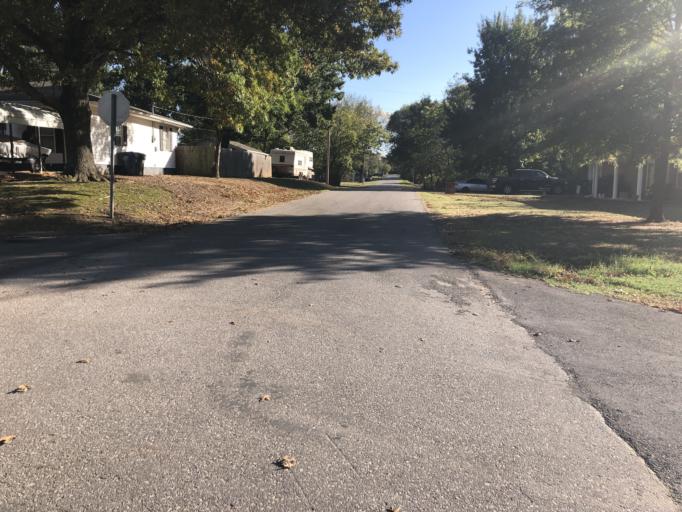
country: US
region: Oklahoma
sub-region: Pottawatomie County
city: Tecumseh
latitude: 35.2566
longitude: -96.9406
